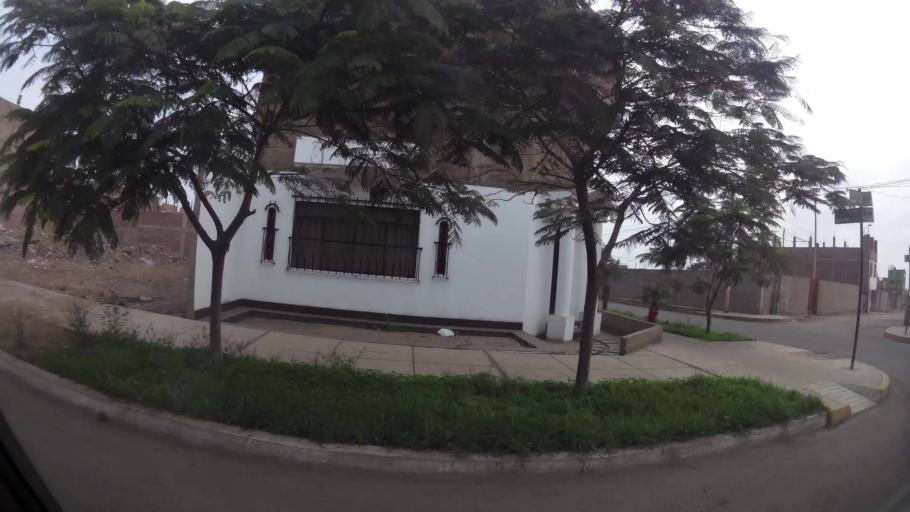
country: PE
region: Lima
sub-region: Provincia de Huaral
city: Huaral
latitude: -11.4933
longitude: -77.2149
